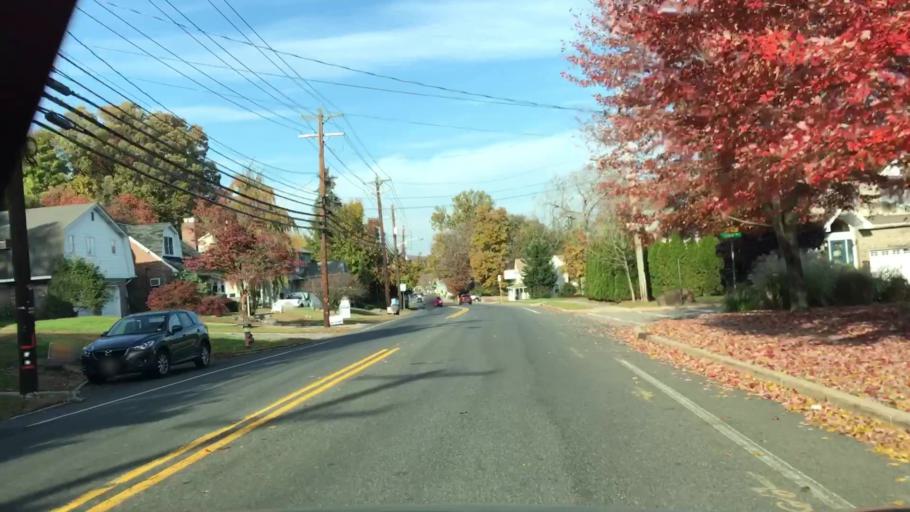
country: US
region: New Jersey
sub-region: Bergen County
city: Northvale
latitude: 41.0031
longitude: -73.9511
